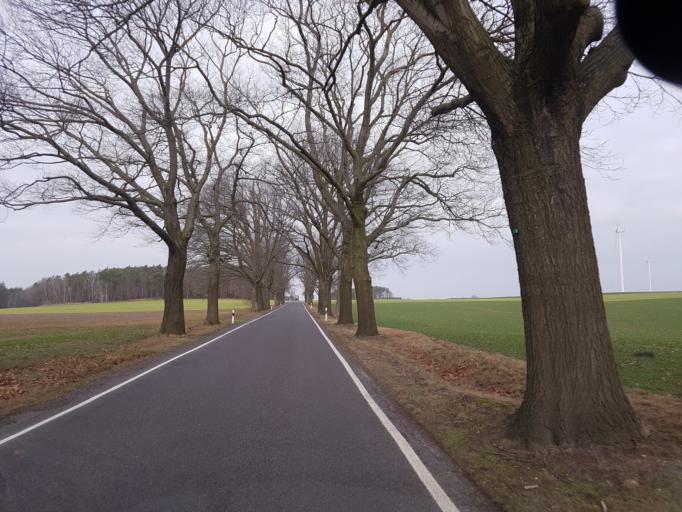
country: DE
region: Brandenburg
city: Hohenbucko
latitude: 51.6960
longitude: 13.5057
